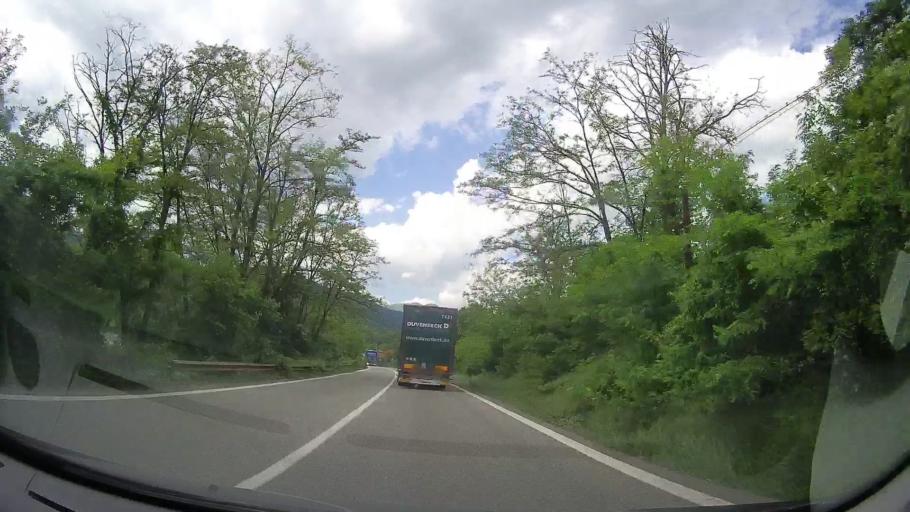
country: RO
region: Valcea
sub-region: Oras Calimanesti
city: Jiblea Veche
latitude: 45.2601
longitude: 24.3332
